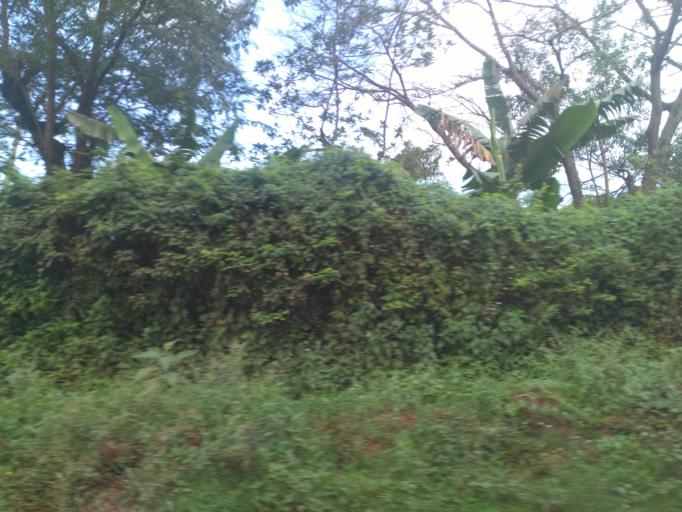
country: UG
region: Central Region
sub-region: Buikwe District
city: Njeru
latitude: 0.3985
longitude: 33.1751
